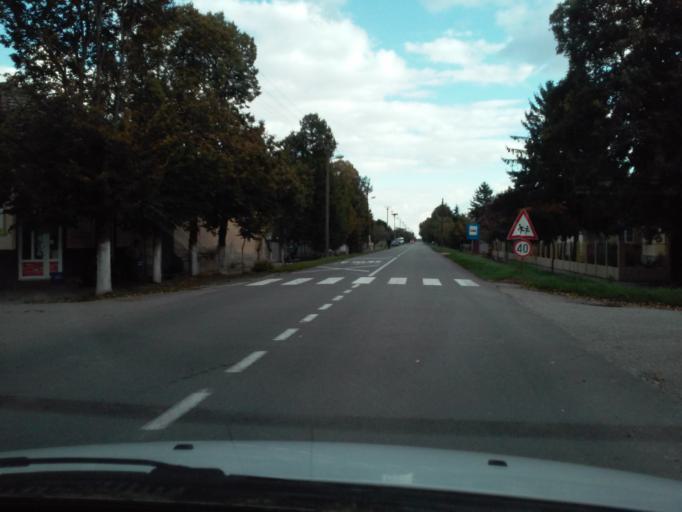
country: RS
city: Sajan
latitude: 45.8413
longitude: 20.2777
